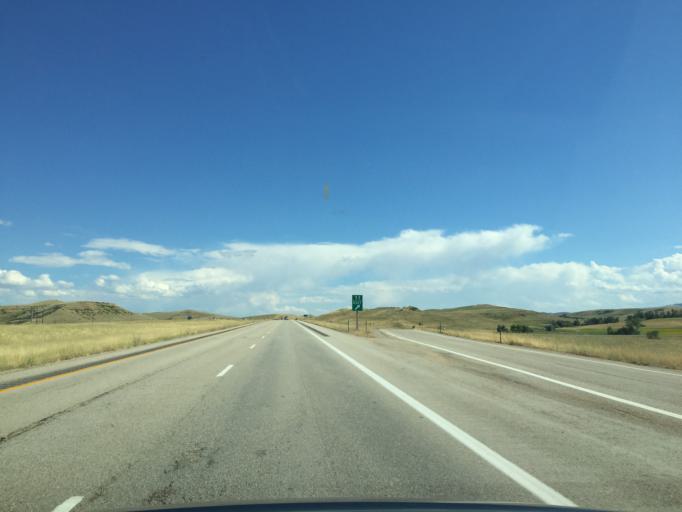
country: US
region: Wyoming
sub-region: Sheridan County
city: Sheridan
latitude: 44.6687
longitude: -106.8829
